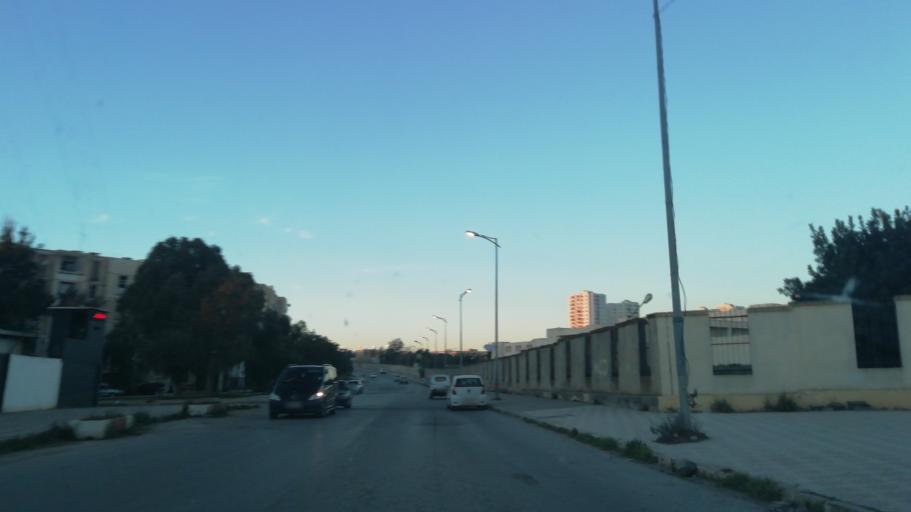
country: DZ
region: Oran
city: Bir el Djir
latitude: 35.7054
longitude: -0.5853
